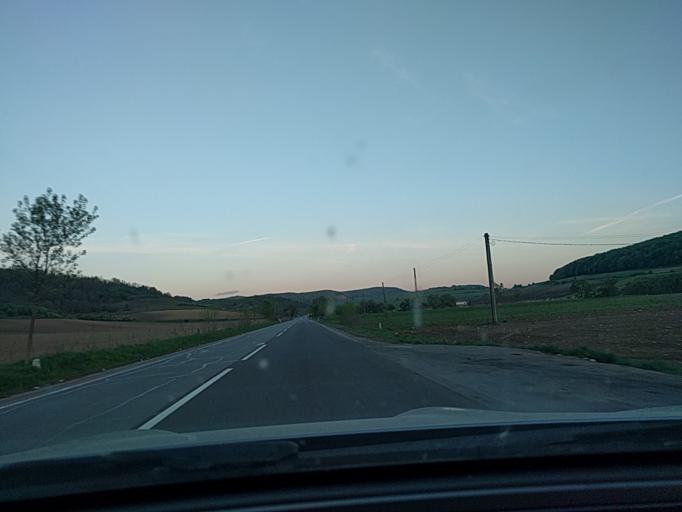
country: RO
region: Mures
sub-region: Comuna Nades
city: Nades
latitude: 46.3252
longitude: 24.7147
